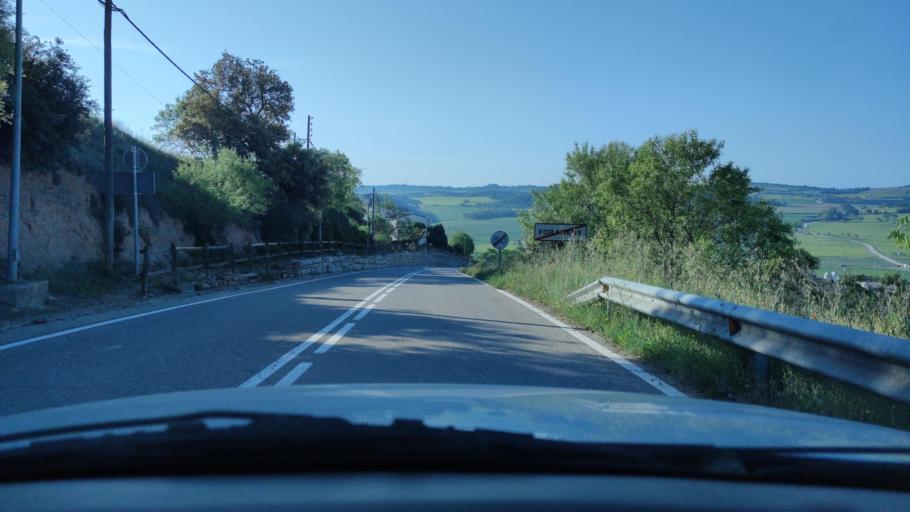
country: ES
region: Catalonia
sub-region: Provincia de Lleida
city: Artesa de Segre
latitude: 41.8762
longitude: 1.0152
